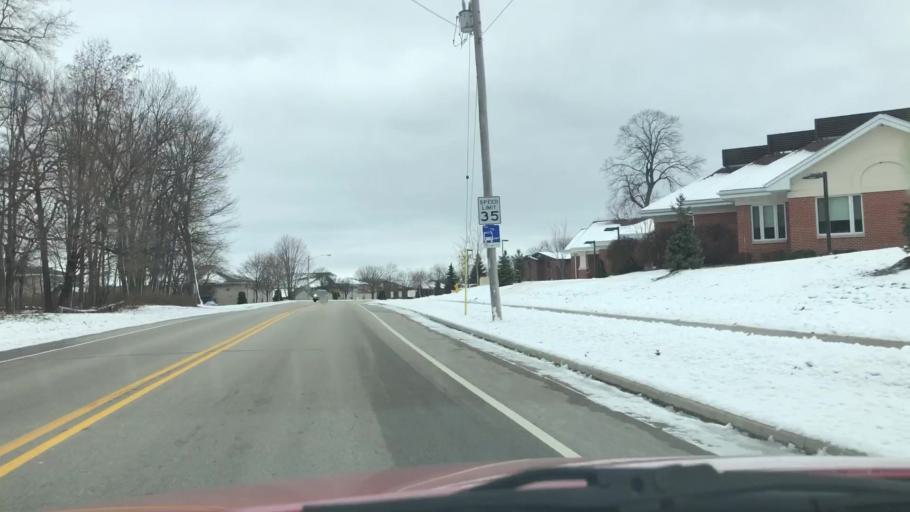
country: US
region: Wisconsin
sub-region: Brown County
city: Ashwaubenon
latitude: 44.4848
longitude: -88.0760
